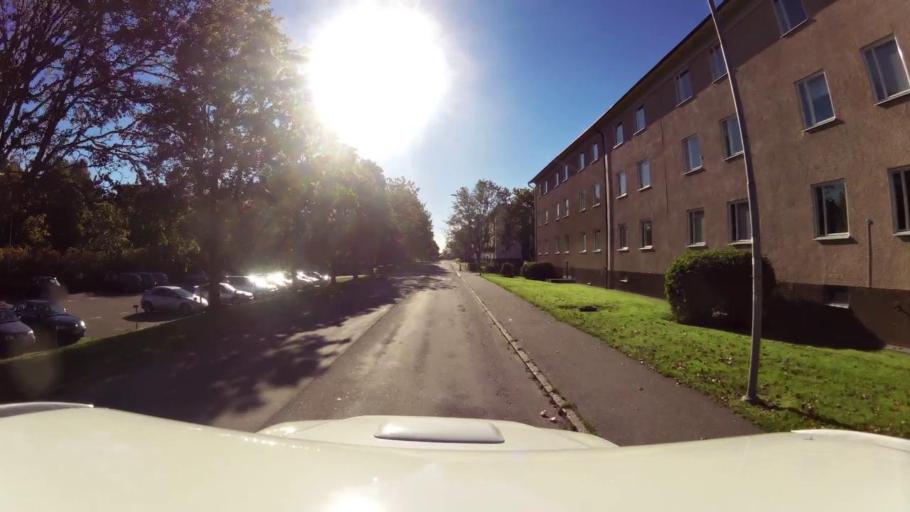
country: SE
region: OEstergoetland
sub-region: Linkopings Kommun
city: Linkoping
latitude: 58.3920
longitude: 15.6460
